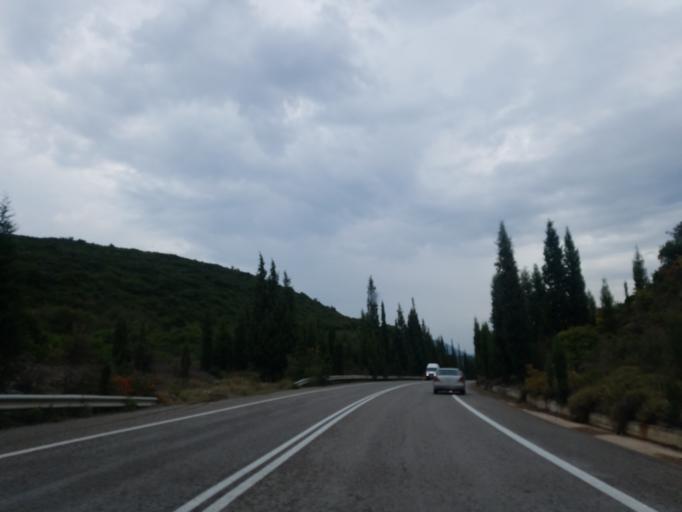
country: GR
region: Central Greece
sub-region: Nomos Voiotias
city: Livadeia
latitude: 38.4435
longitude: 22.8055
